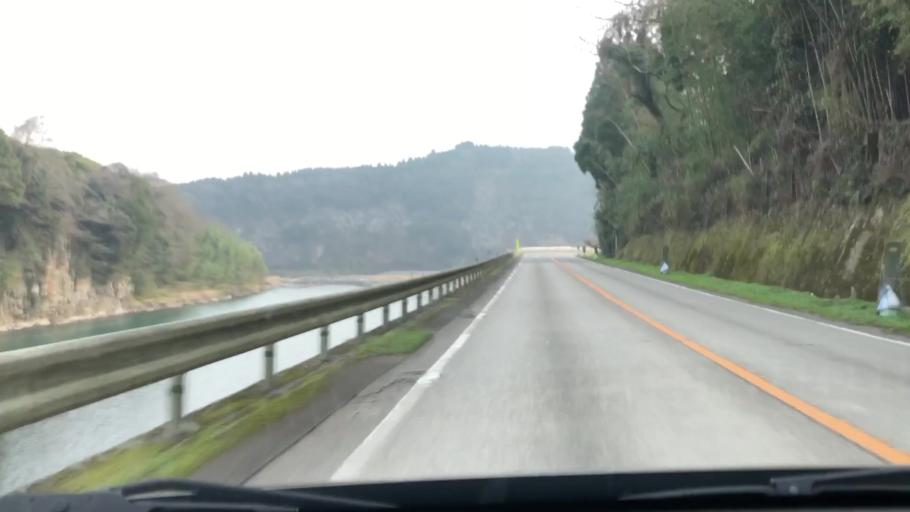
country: JP
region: Oita
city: Takedamachi
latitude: 32.9829
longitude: 131.5445
